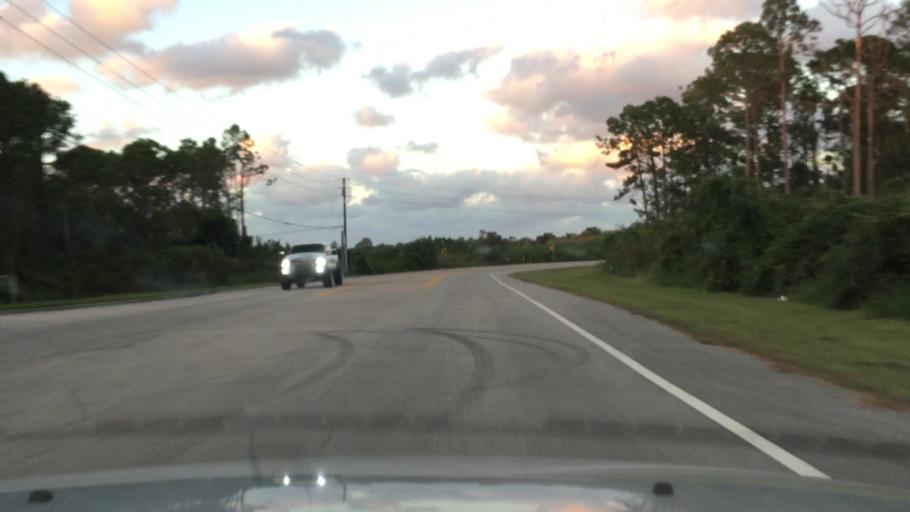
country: US
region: Florida
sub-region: Volusia County
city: Ormond Beach
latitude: 29.2894
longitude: -81.1130
